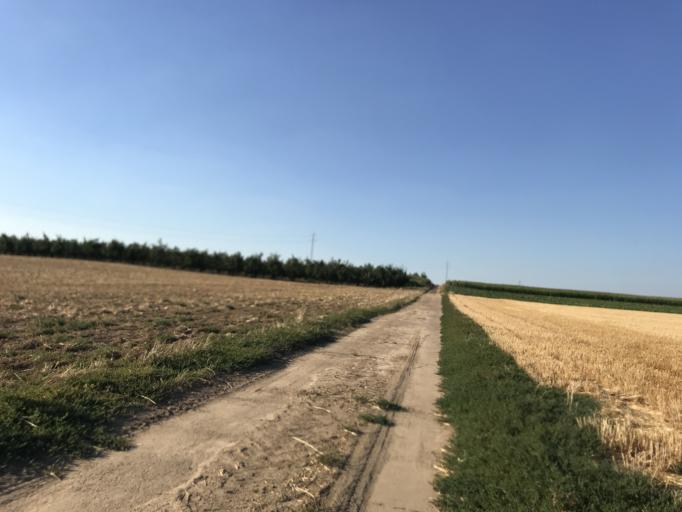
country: DE
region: Rheinland-Pfalz
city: Essenheim
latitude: 49.9384
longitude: 8.1364
